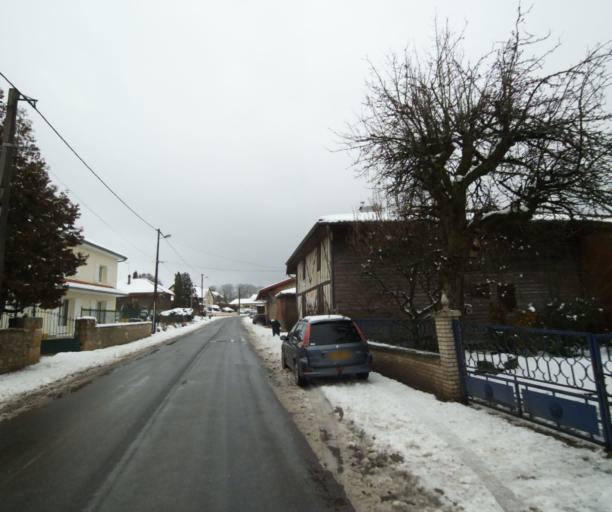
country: FR
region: Champagne-Ardenne
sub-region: Departement de la Haute-Marne
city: Laneuville-a-Remy
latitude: 48.4633
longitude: 4.8416
